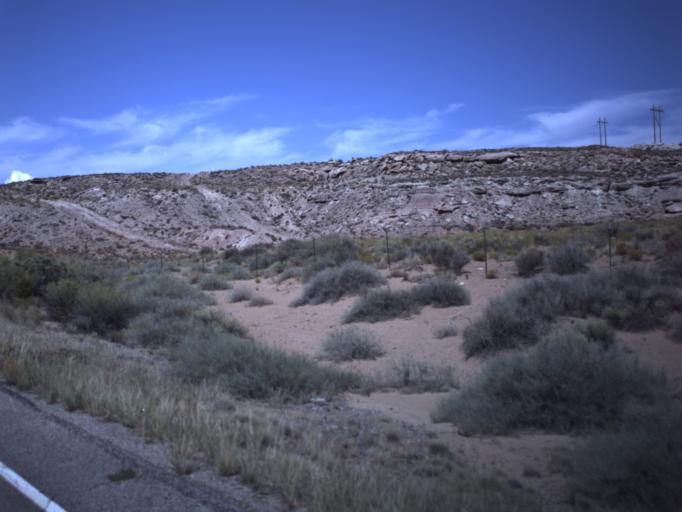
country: US
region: Utah
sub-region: San Juan County
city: Blanding
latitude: 37.2734
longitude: -109.3453
